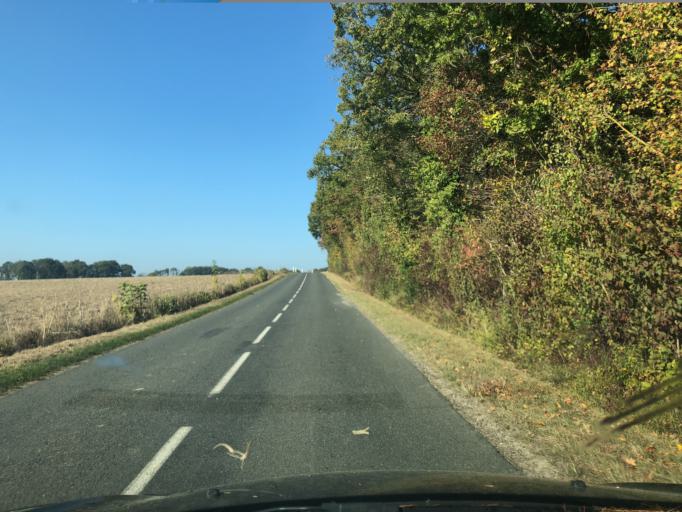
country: FR
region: Centre
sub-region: Departement d'Indre-et-Loire
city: Neuvy-le-Roi
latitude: 47.5673
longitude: 0.6029
